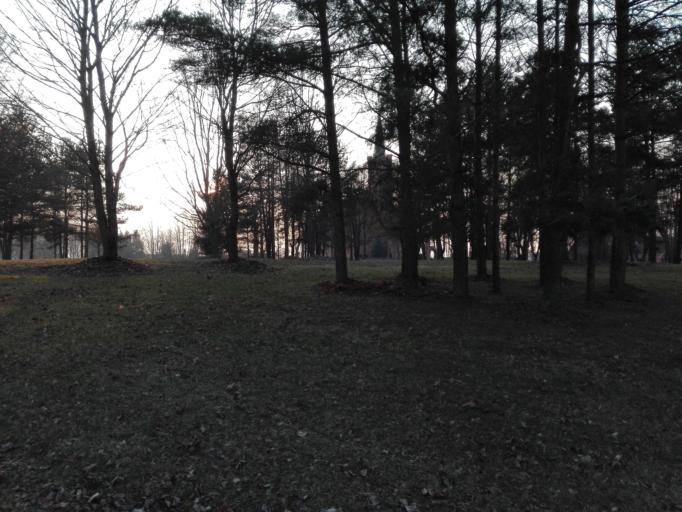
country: LT
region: Panevezys
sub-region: Birzai
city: Birzai
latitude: 56.2076
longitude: 24.7613
